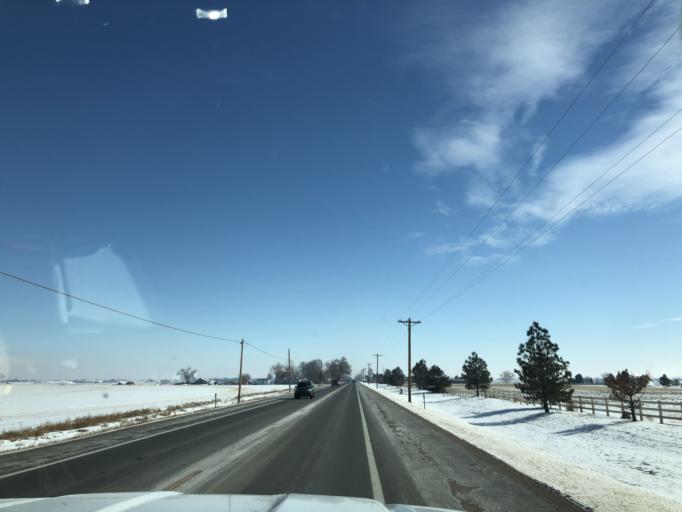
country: US
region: Colorado
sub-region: Morgan County
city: Fort Morgan
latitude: 40.2540
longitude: -103.8454
